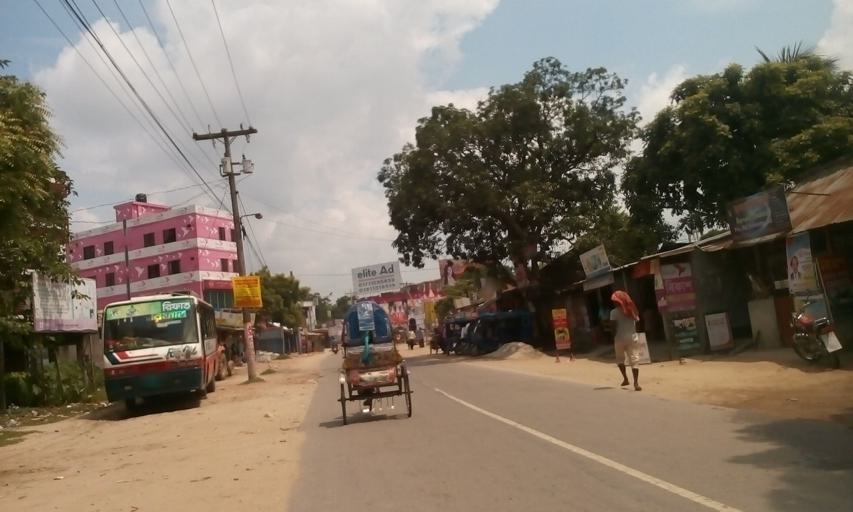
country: IN
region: West Bengal
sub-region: Dakshin Dinajpur
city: Balurghat
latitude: 25.3916
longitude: 88.9910
